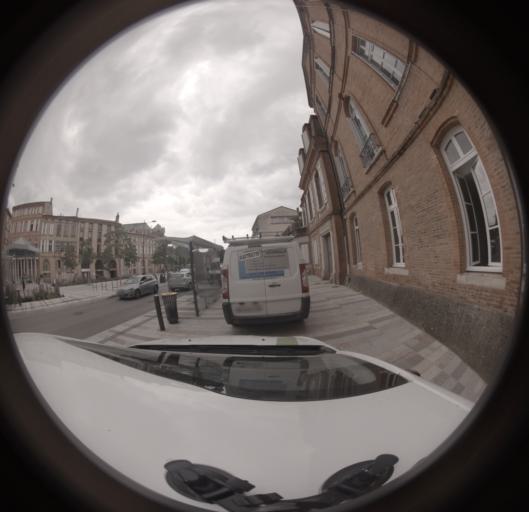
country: FR
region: Midi-Pyrenees
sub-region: Departement du Tarn-et-Garonne
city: Montauban
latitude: 44.0141
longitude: 1.3555
